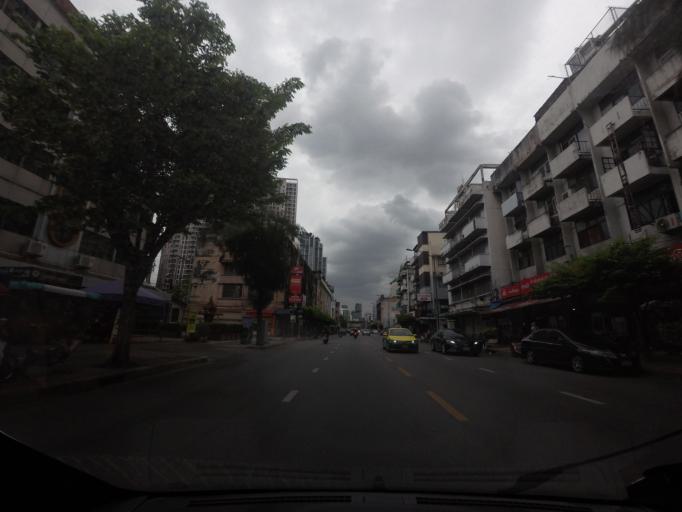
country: TH
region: Bangkok
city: Phaya Thai
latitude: 13.7906
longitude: 100.5443
